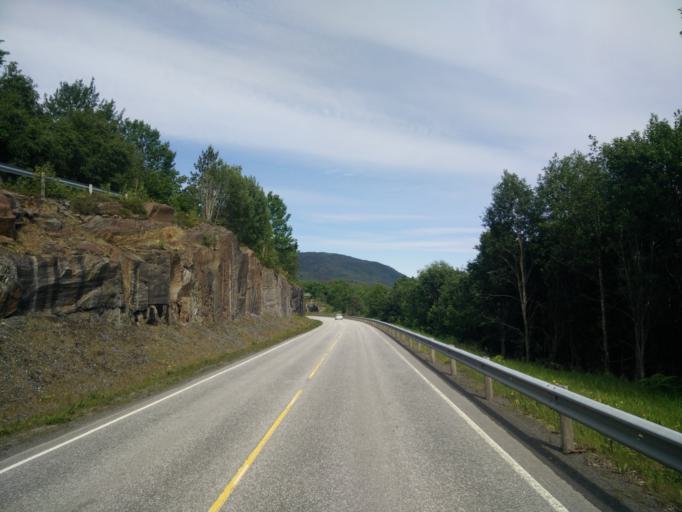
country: NO
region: More og Romsdal
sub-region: Kristiansund
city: Rensvik
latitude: 62.9785
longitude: 7.8657
